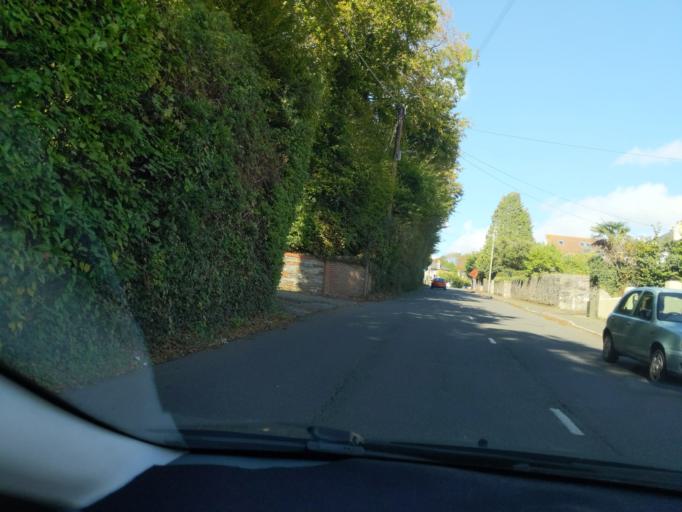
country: GB
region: England
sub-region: Plymouth
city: Plymstock
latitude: 50.3567
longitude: -4.0731
